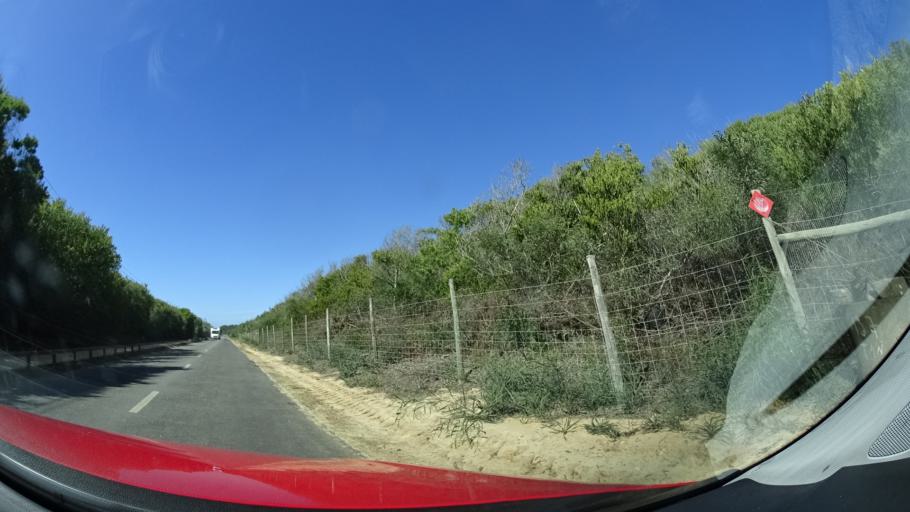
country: PT
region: Beja
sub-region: Odemira
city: Sao Teotonio
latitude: 37.5424
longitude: -8.7875
